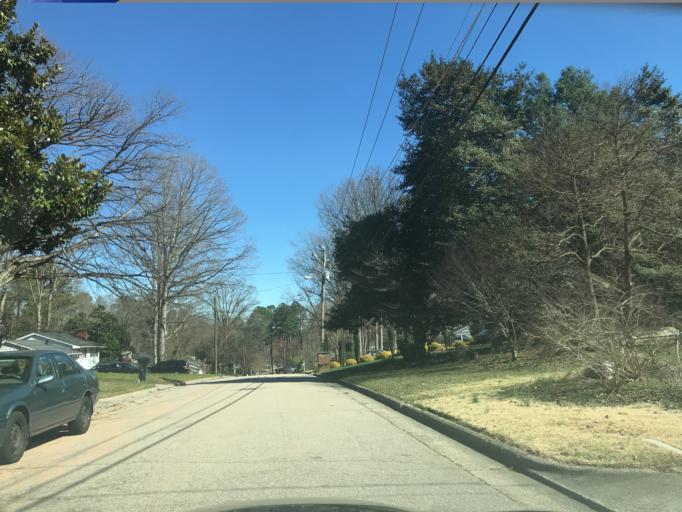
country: US
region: North Carolina
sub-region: Wake County
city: West Raleigh
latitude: 35.8485
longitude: -78.6433
